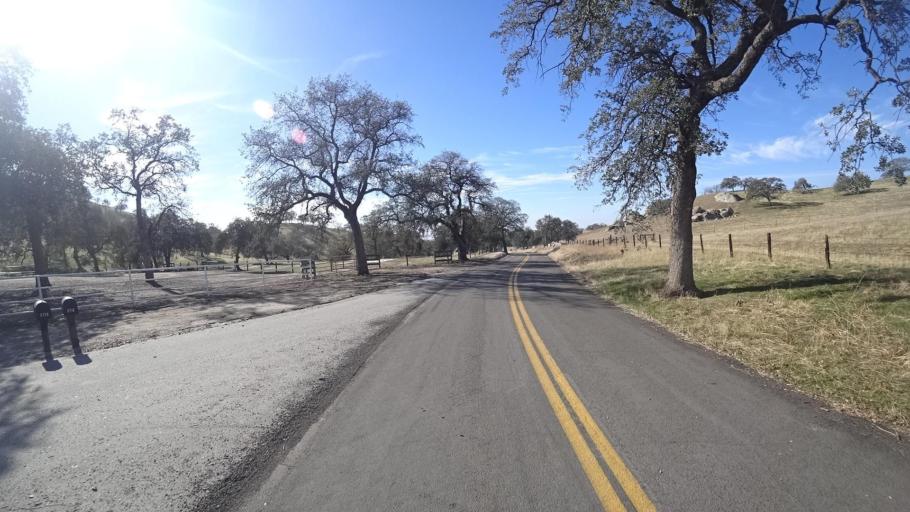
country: US
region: California
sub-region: Tulare County
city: Richgrove
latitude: 35.6781
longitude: -118.8461
